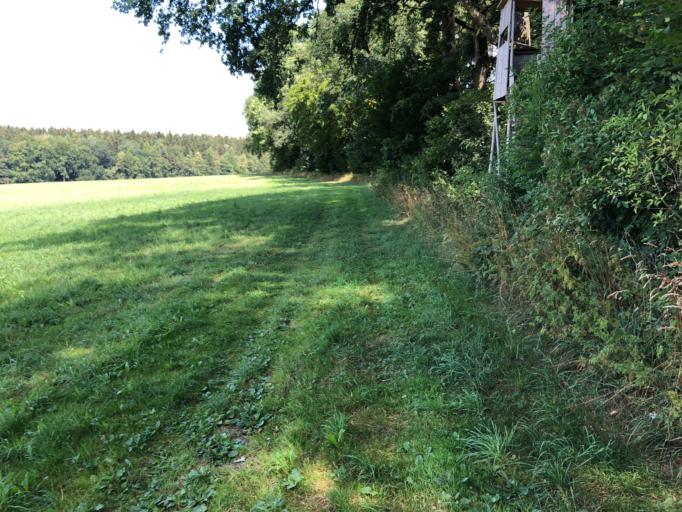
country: DE
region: Baden-Wuerttemberg
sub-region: Tuebingen Region
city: Unlingen
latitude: 48.1761
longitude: 9.5492
